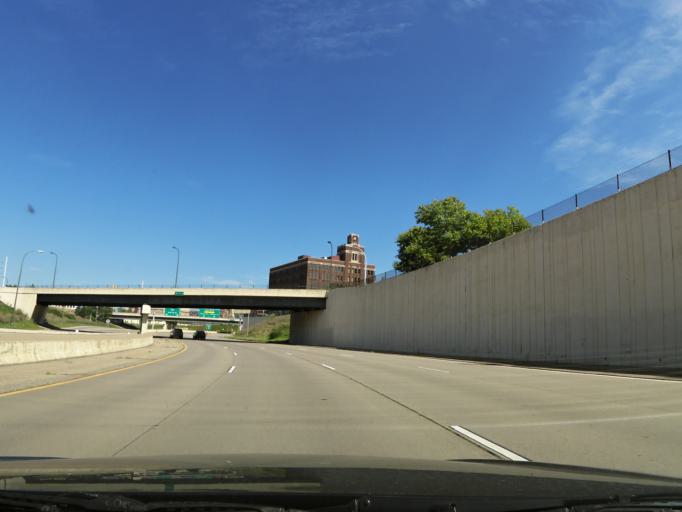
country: US
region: Minnesota
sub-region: Hennepin County
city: Minneapolis
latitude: 44.9764
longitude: -93.2811
